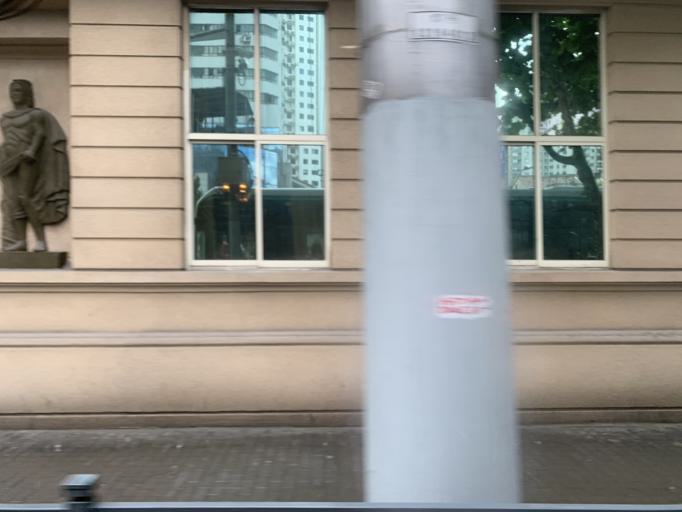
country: CN
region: Shanghai Shi
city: Luwan
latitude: 31.2138
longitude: 121.4802
